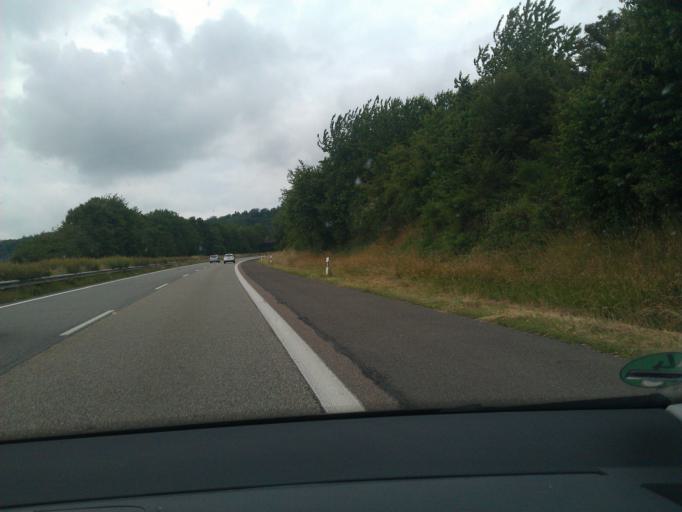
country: DE
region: Rheinland-Pfalz
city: Konken
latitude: 49.5174
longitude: 7.3430
